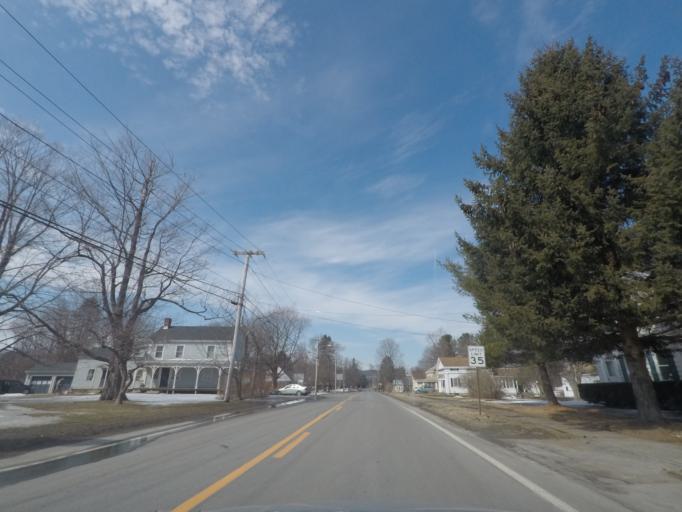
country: US
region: Massachusetts
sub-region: Berkshire County
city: West Stockbridge
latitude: 42.3371
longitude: -73.3705
